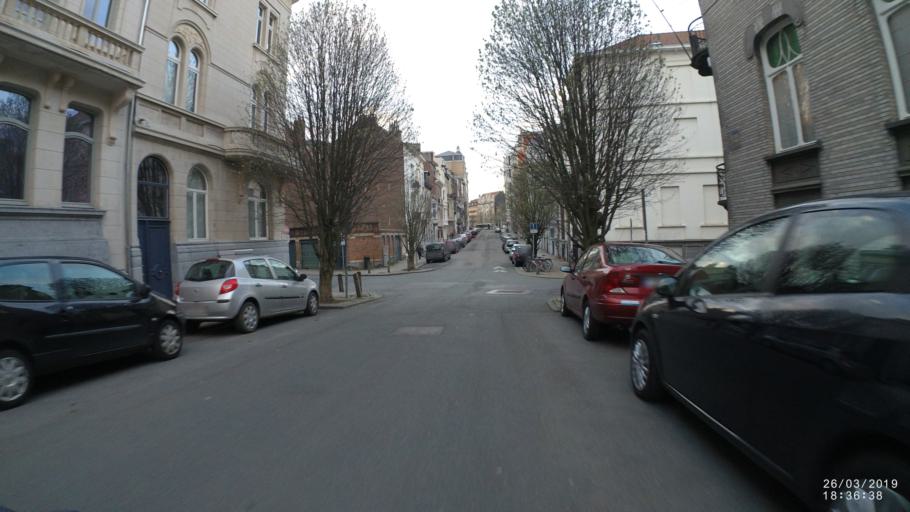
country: BE
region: Brussels Capital
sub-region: Bruxelles-Capitale
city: Brussels
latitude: 50.8373
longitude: 4.4027
